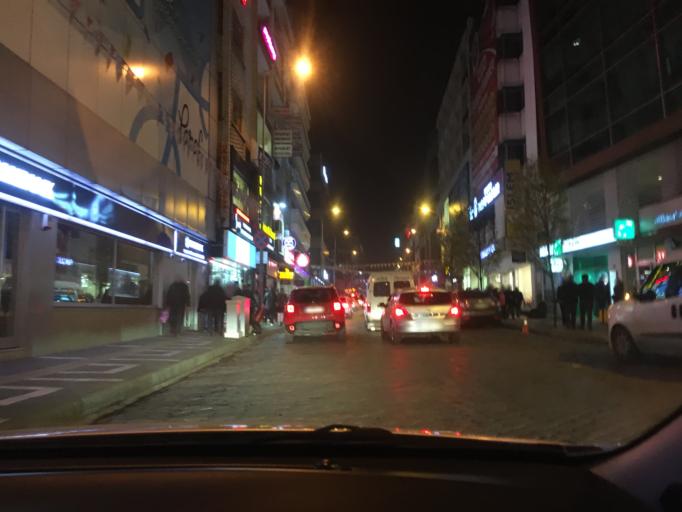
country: TR
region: Trabzon
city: Trabzon
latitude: 41.0064
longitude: 39.7261
